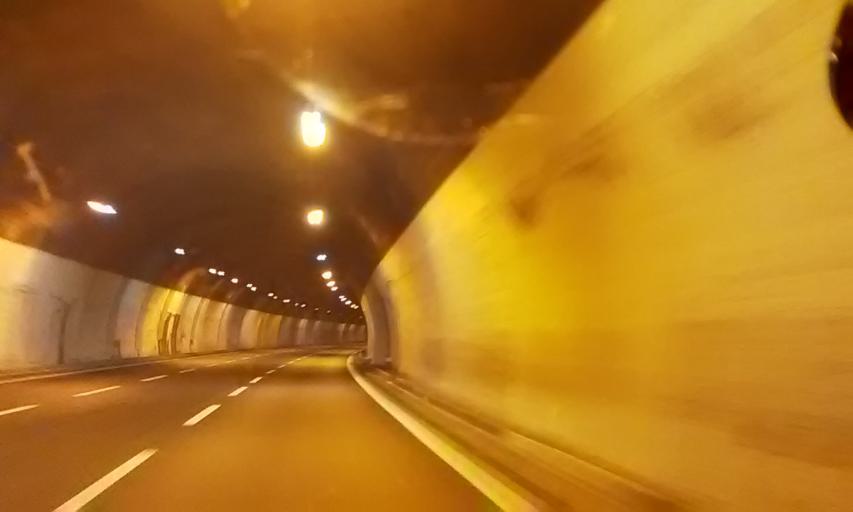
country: IT
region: Liguria
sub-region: Provincia di Genova
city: Rossiglione
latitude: 44.5635
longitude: 8.6645
